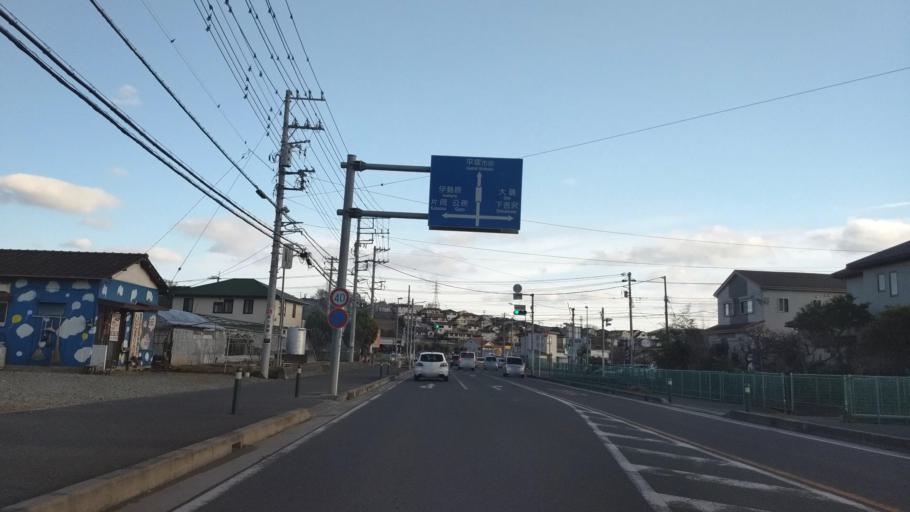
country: JP
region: Kanagawa
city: Oiso
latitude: 35.3426
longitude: 139.2930
